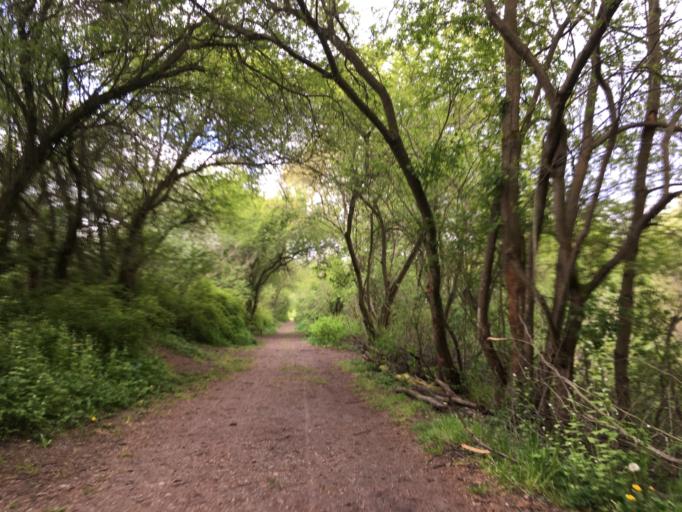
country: DE
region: Berlin
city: Blankenfelde
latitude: 52.6264
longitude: 13.4044
